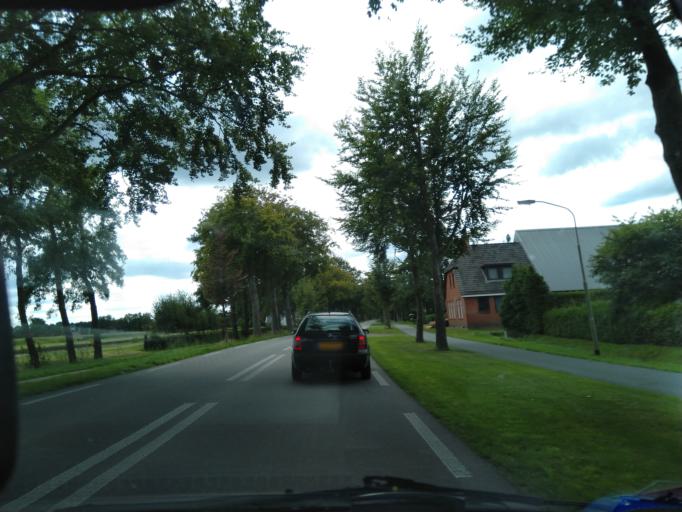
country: NL
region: Drenthe
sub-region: Gemeente Tynaarlo
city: Tynaarlo
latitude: 53.1032
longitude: 6.6035
